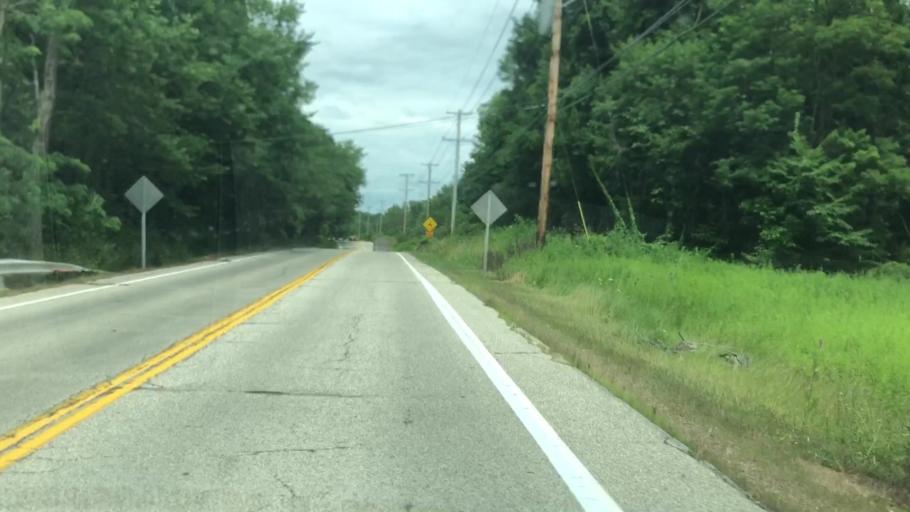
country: US
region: Ohio
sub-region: Summit County
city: Fairlawn
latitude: 41.1715
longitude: -81.5614
